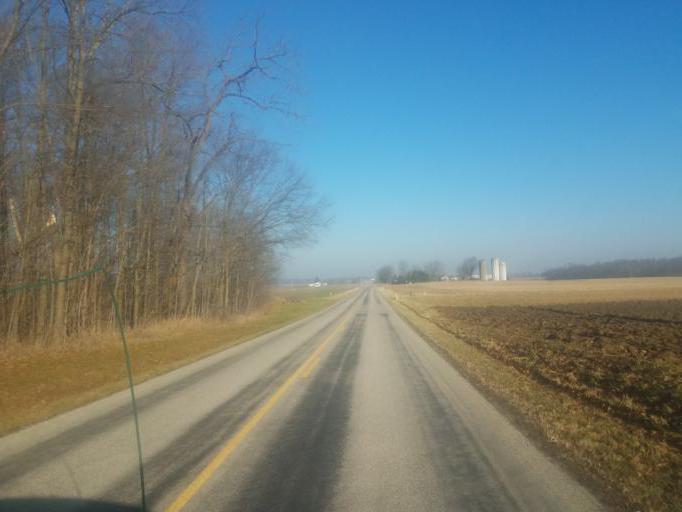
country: US
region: Ohio
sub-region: Crawford County
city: Bucyrus
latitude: 40.8697
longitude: -82.9401
